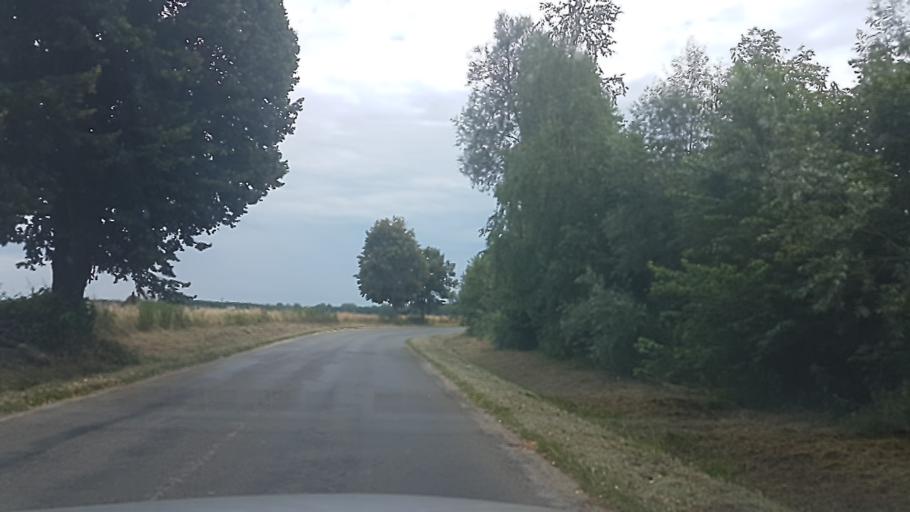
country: HU
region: Somogy
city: Barcs
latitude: 45.9603
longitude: 17.5949
